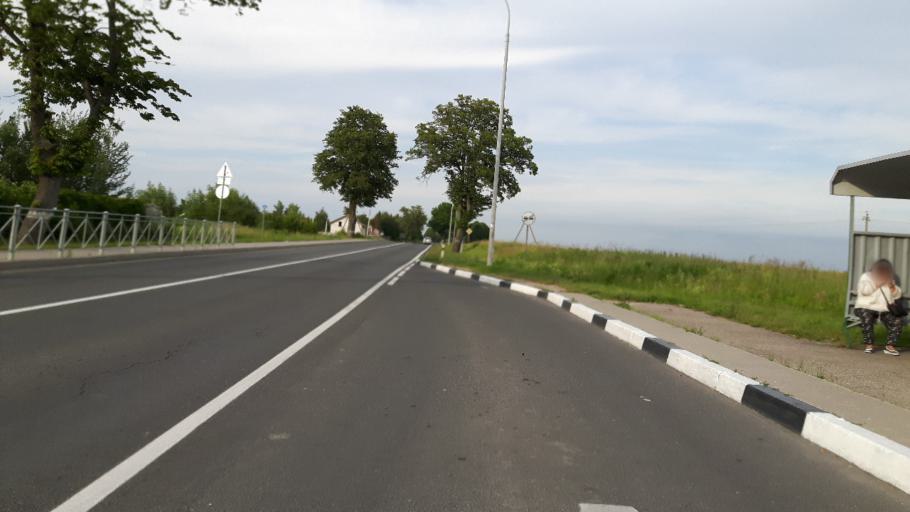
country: RU
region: Kaliningrad
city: Vzmorye
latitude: 54.6142
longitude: 20.2544
